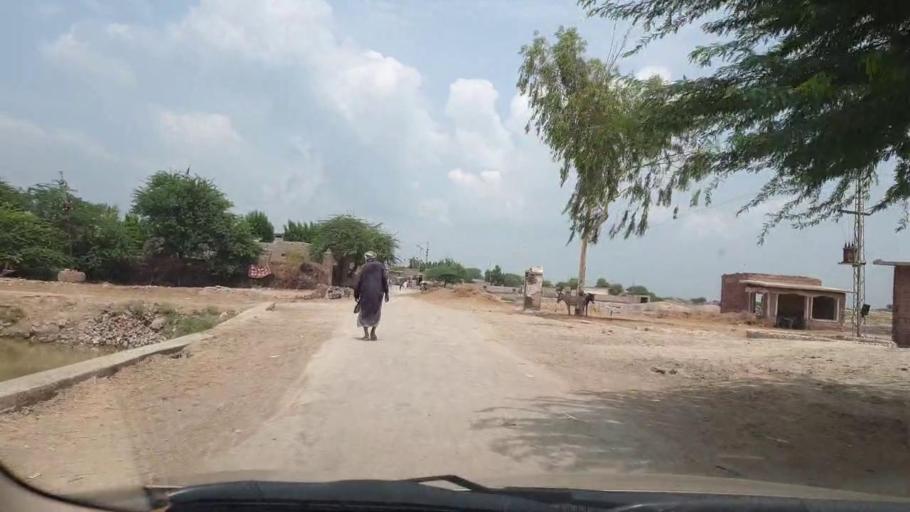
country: PK
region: Sindh
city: Larkana
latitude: 27.5589
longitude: 68.1235
